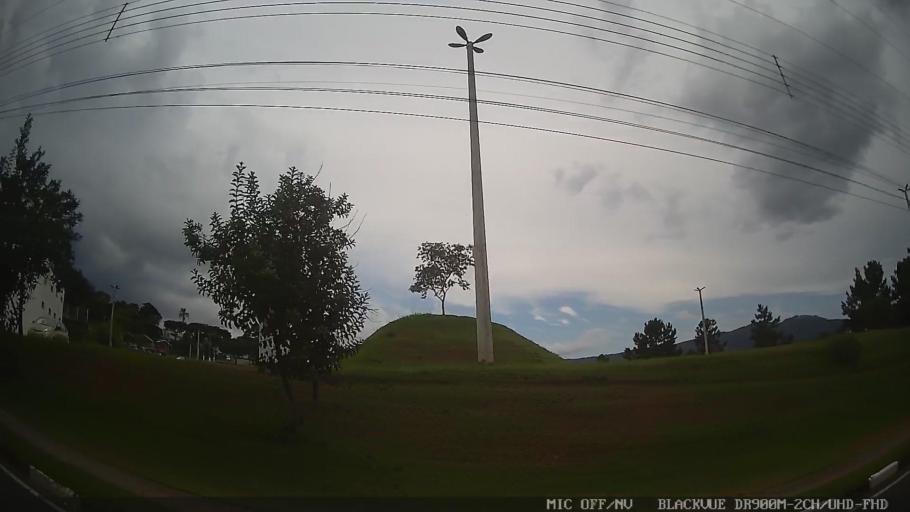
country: BR
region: Sao Paulo
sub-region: Atibaia
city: Atibaia
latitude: -23.1186
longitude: -46.5475
